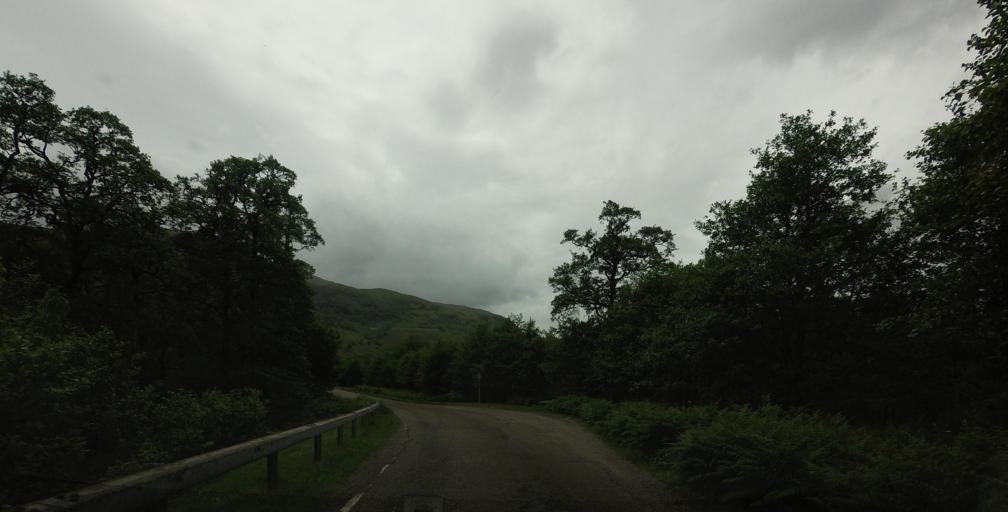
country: GB
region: Scotland
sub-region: Highland
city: Fort William
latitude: 56.7668
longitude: -5.2410
